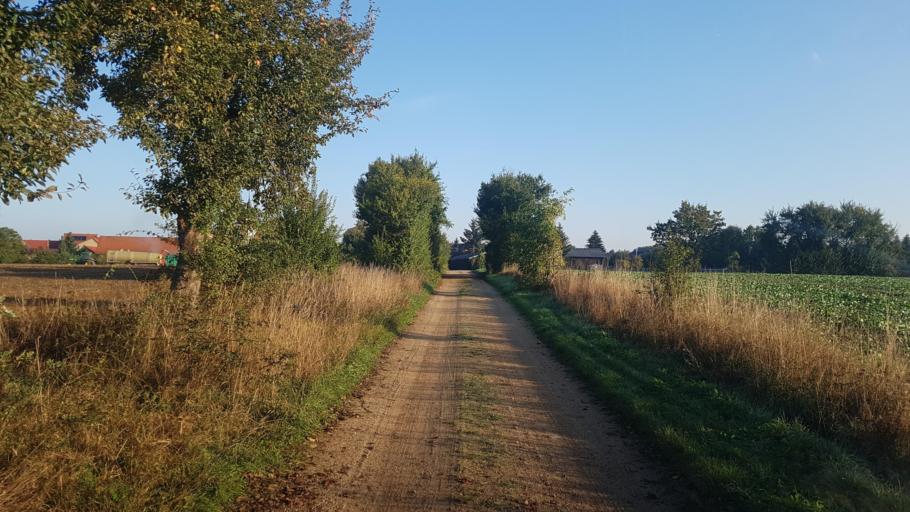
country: DE
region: Brandenburg
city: Lebusa
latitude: 51.8125
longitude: 13.4509
